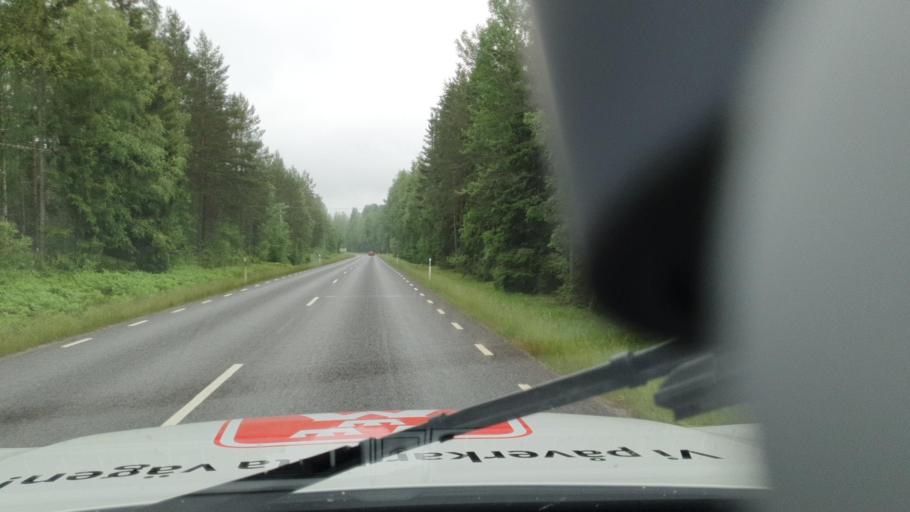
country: SE
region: Vaermland
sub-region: Kristinehamns Kommun
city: Bjorneborg
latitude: 59.2238
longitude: 14.3100
